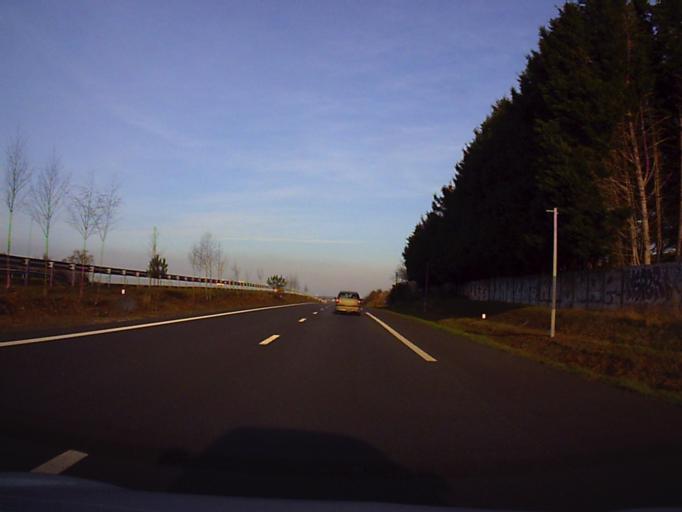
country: FR
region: Brittany
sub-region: Departement d'Ille-et-Vilaine
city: Saint-Thurial
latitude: 48.0523
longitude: -1.9192
